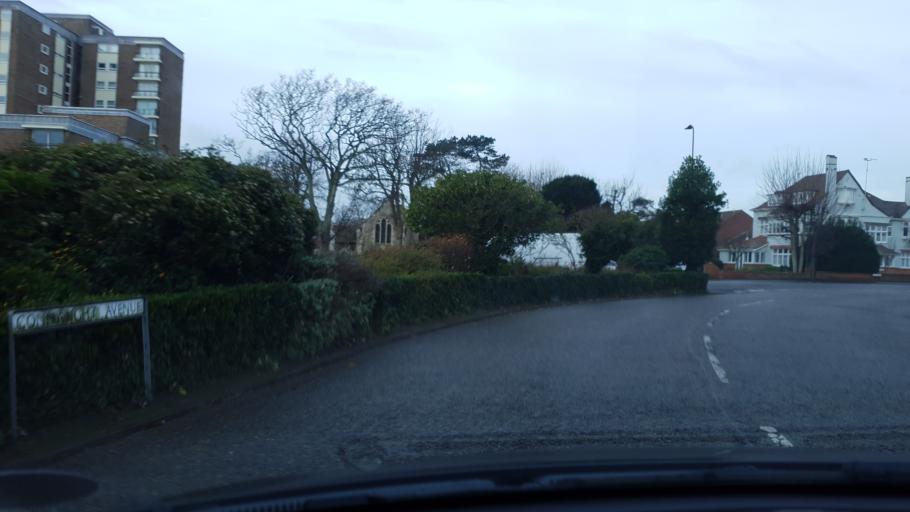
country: GB
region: England
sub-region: Essex
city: Frinton-on-Sea
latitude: 51.8293
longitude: 1.2466
